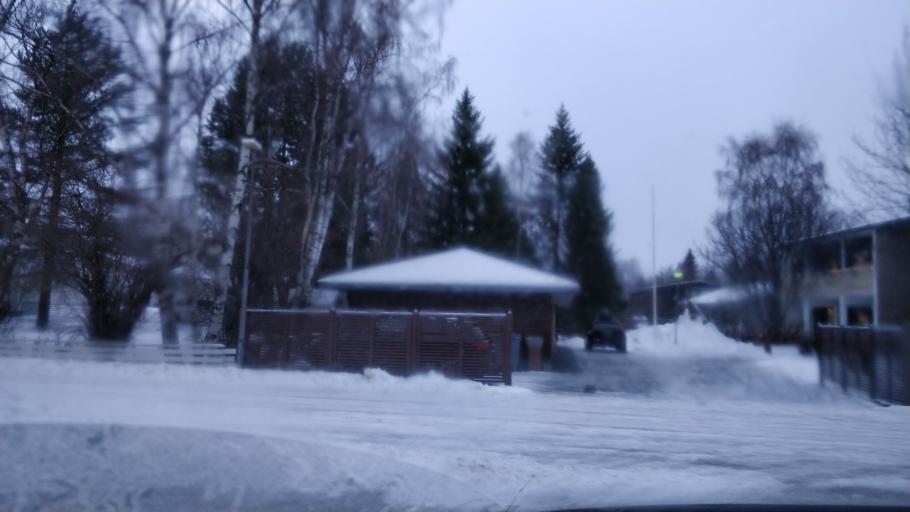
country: FI
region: Lapland
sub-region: Kemi-Tornio
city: Kemi
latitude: 65.7421
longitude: 24.5636
